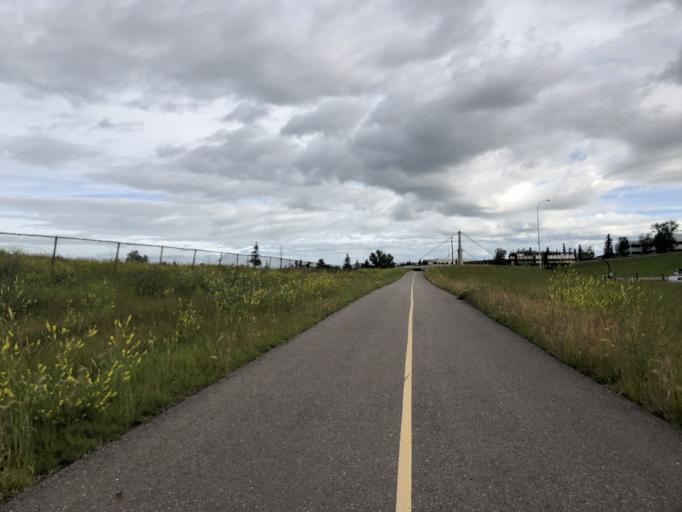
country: CA
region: Alberta
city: Calgary
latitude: 51.0723
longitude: -114.0277
